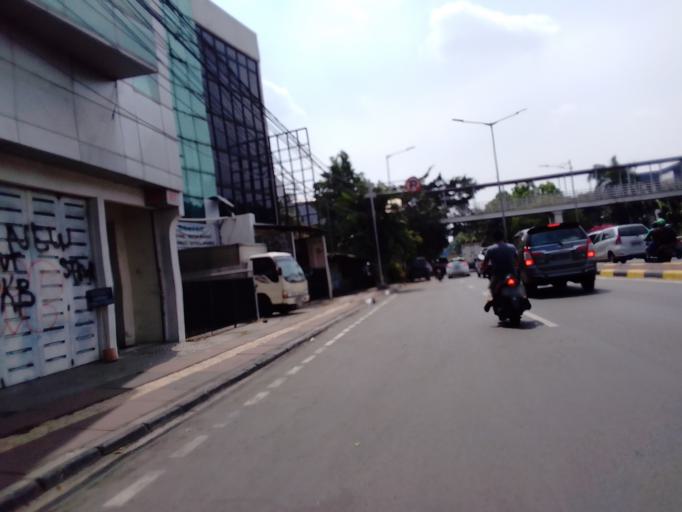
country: ID
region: Jakarta Raya
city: Jakarta
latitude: -6.1801
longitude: 106.8129
